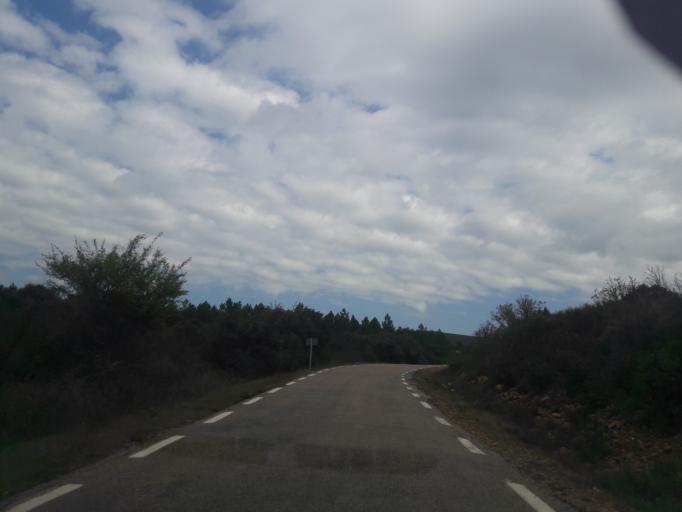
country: ES
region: Castille and Leon
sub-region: Provincia de Salamanca
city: Serradilla del Arroyo
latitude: 40.5327
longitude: -6.3837
